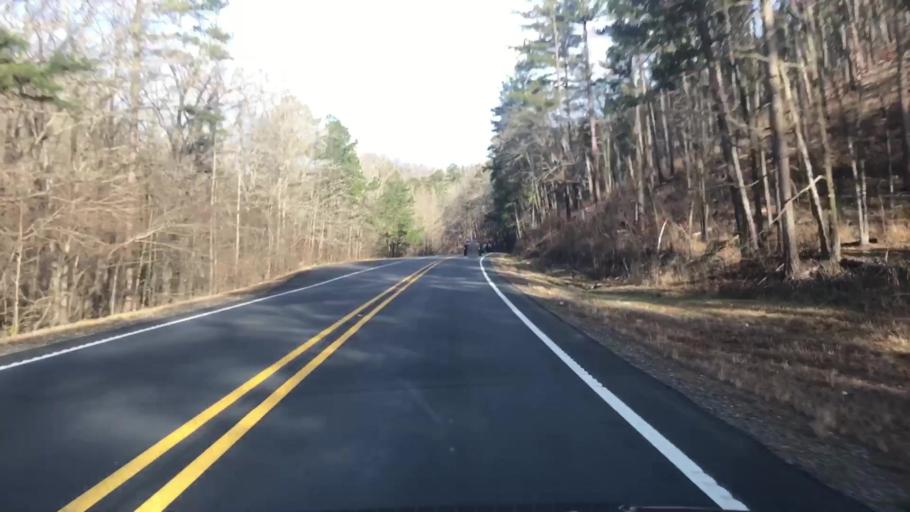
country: US
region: Arkansas
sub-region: Montgomery County
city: Mount Ida
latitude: 34.5207
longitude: -93.3897
